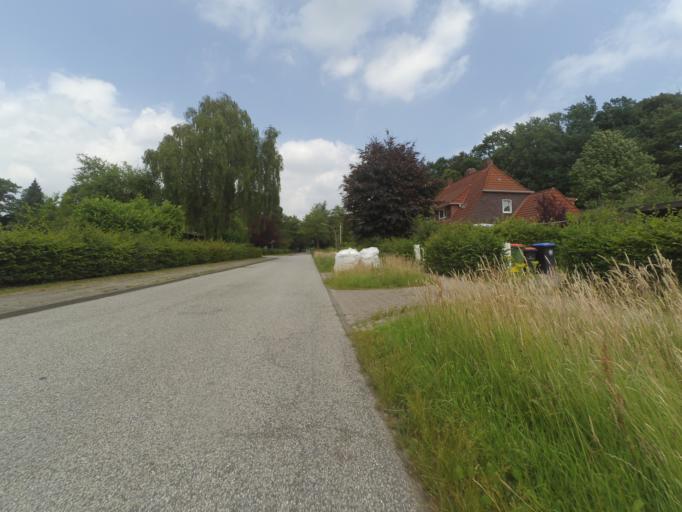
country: DE
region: Hamburg
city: Sasel
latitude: 53.6324
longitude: 10.1249
